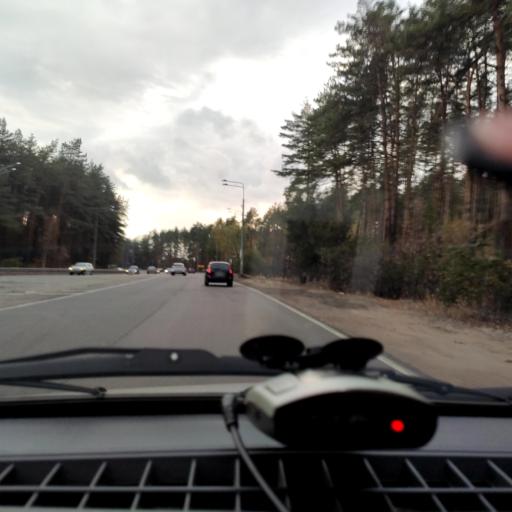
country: RU
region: Voronezj
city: Podgornoye
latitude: 51.7358
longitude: 39.1756
